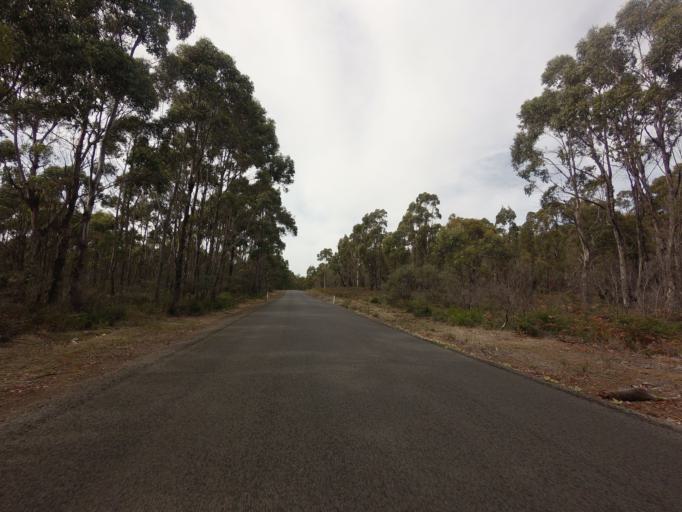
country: AU
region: Tasmania
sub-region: Sorell
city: Sorell
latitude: -42.5187
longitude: 147.6496
